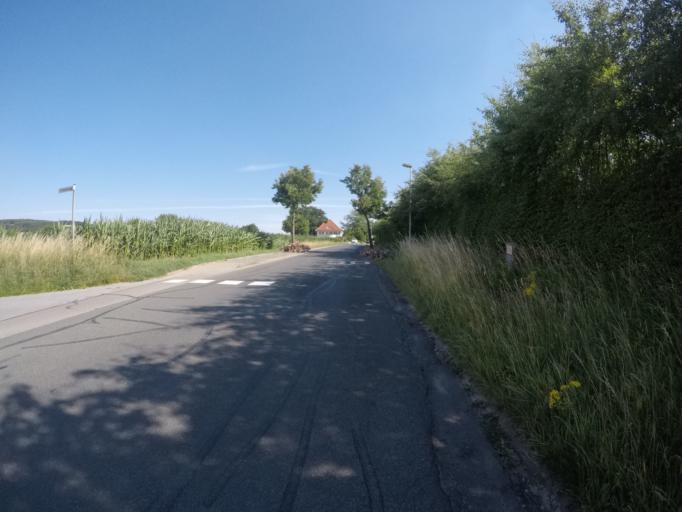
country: DE
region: North Rhine-Westphalia
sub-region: Regierungsbezirk Detmold
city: Herford
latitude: 52.1537
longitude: 8.6694
